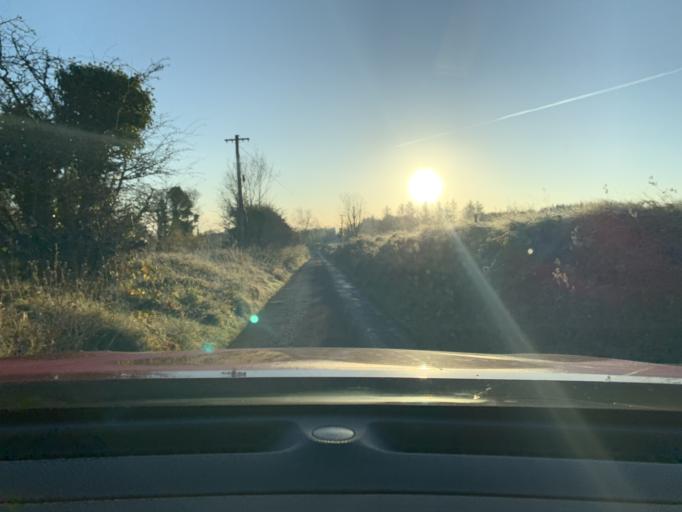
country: IE
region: Connaught
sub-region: Sligo
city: Ballymote
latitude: 53.9875
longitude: -8.5278
